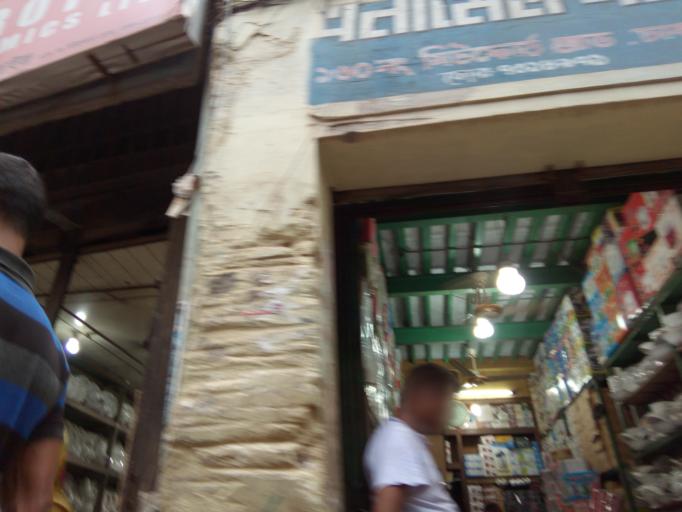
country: BD
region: Dhaka
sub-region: Dhaka
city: Dhaka
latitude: 23.7135
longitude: 90.3991
